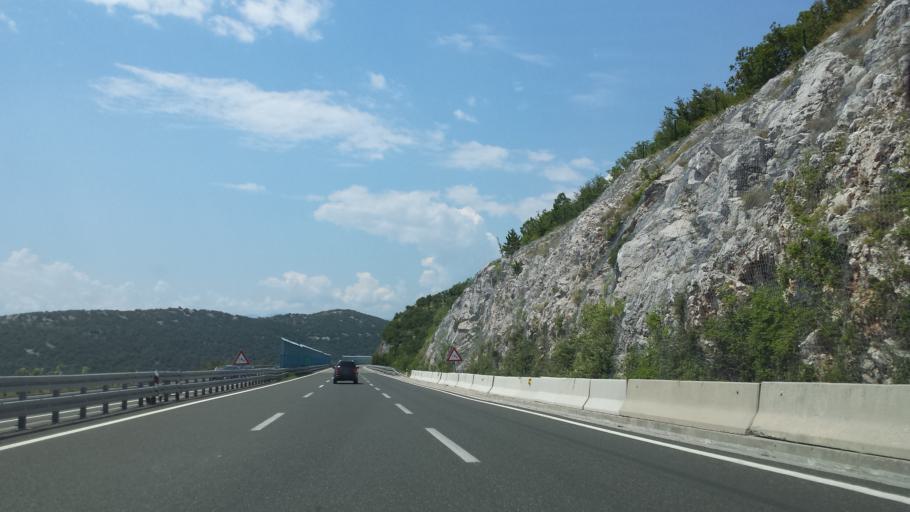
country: HR
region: Primorsko-Goranska
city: Krasica
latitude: 45.3623
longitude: 14.5649
